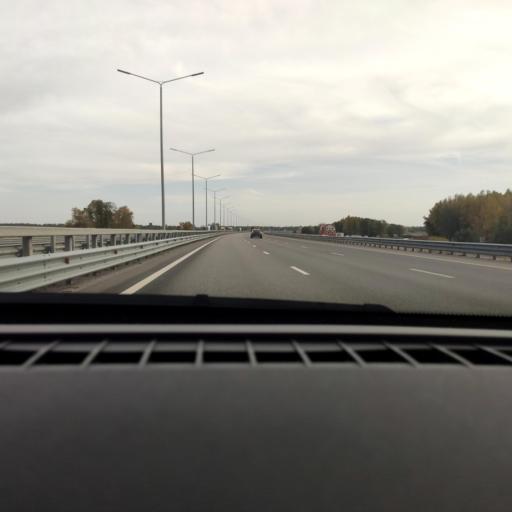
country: RU
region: Voronezj
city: Somovo
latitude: 51.7901
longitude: 39.2769
